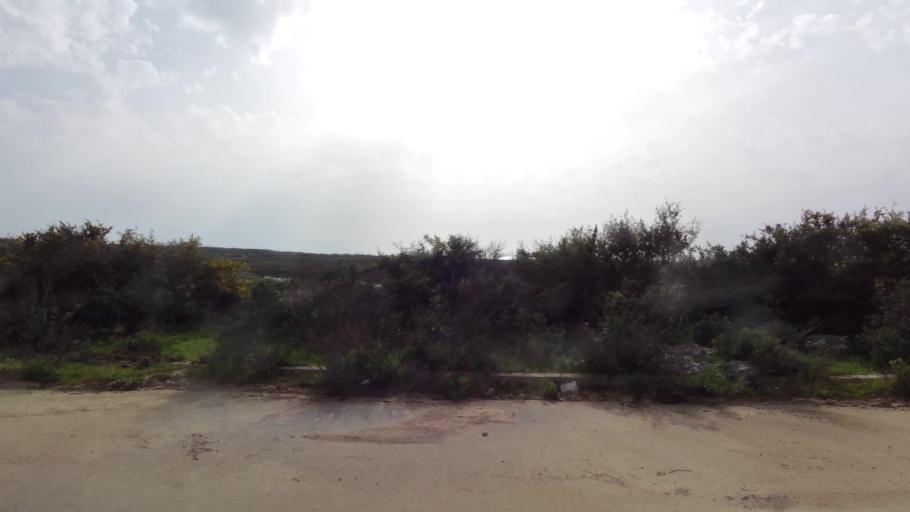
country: MA
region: Tanger-Tetouan
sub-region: Tanger-Assilah
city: Boukhalef
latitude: 35.6959
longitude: -5.9410
